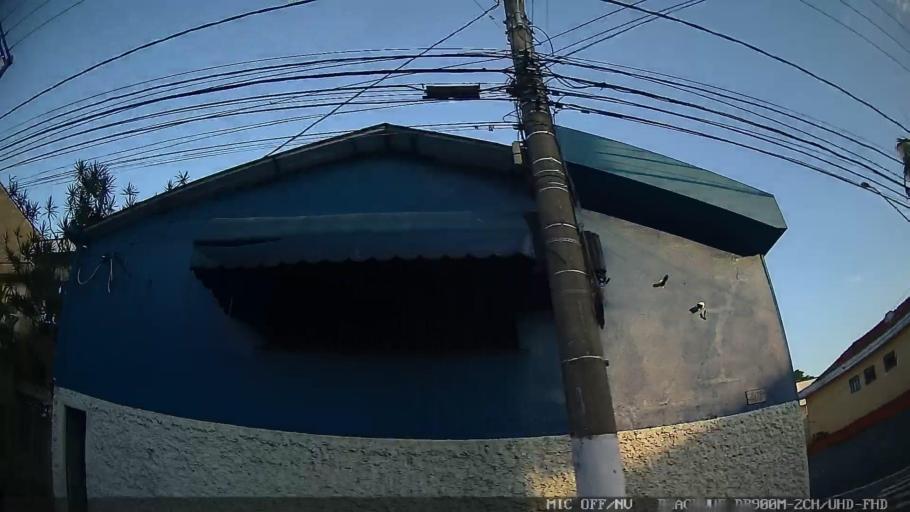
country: BR
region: Sao Paulo
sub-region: Sao Caetano Do Sul
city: Sao Caetano do Sul
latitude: -23.5830
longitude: -46.5412
